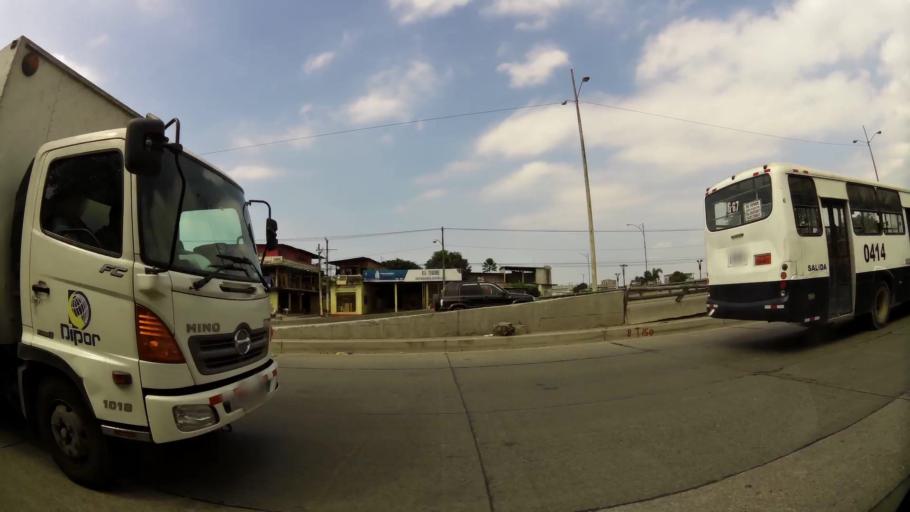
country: EC
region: Guayas
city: Santa Lucia
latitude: -2.0901
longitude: -79.9373
